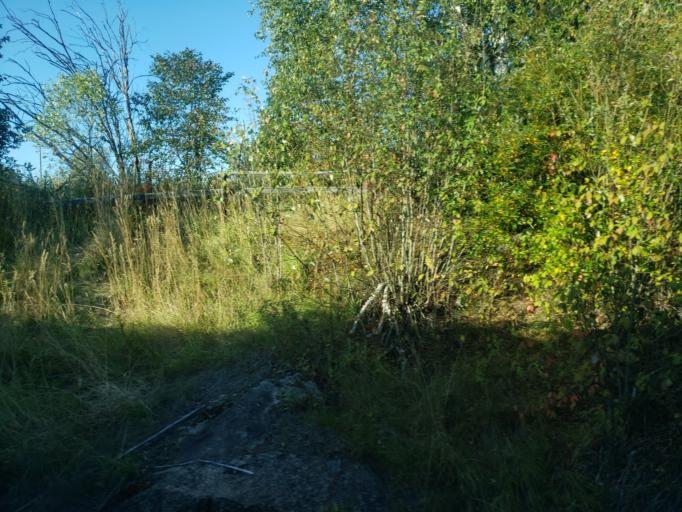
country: FI
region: South Karelia
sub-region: Lappeenranta
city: Lappeenranta
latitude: 60.8686
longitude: 28.2853
